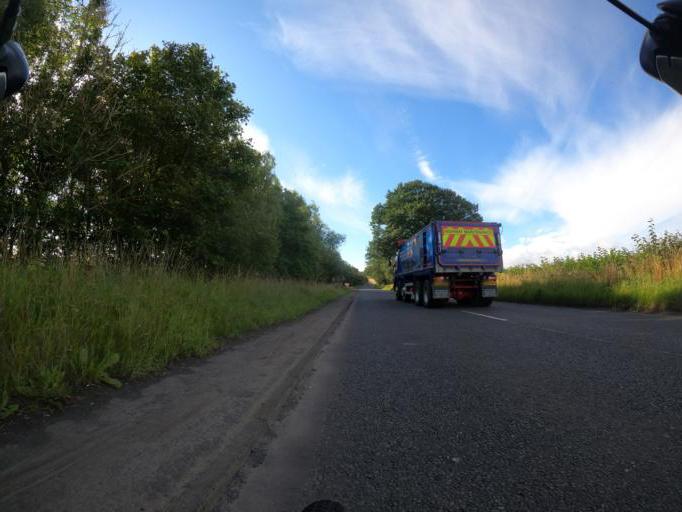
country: GB
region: Scotland
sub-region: Edinburgh
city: Newbridge
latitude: 55.9200
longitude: -3.4105
